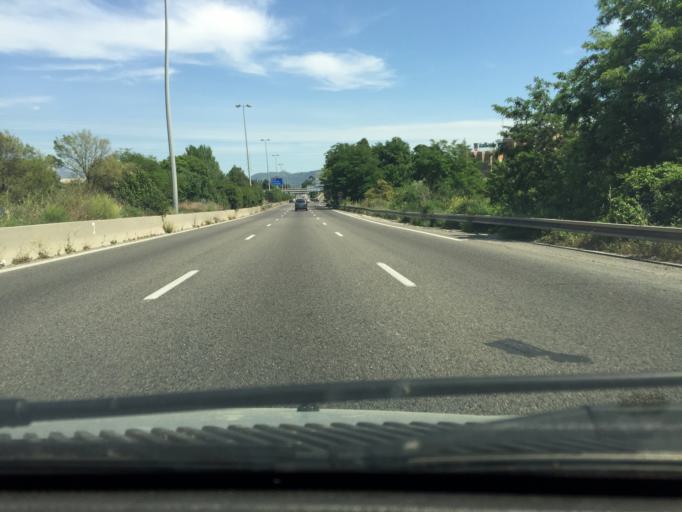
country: FR
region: Provence-Alpes-Cote d'Azur
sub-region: Departement des Bouches-du-Rhone
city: Marseille 11
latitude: 43.2937
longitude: 5.4723
